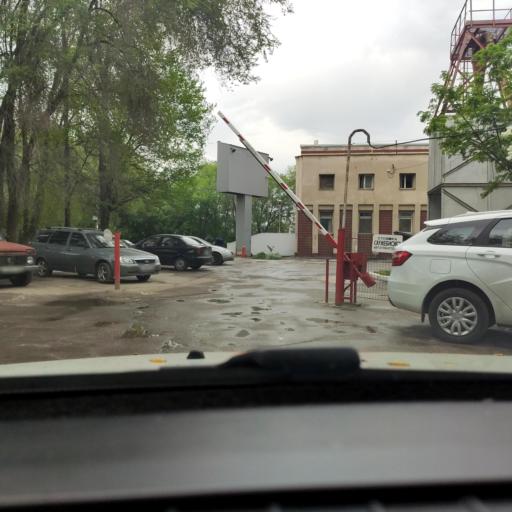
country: RU
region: Samara
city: Smyshlyayevka
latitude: 53.2132
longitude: 50.2830
